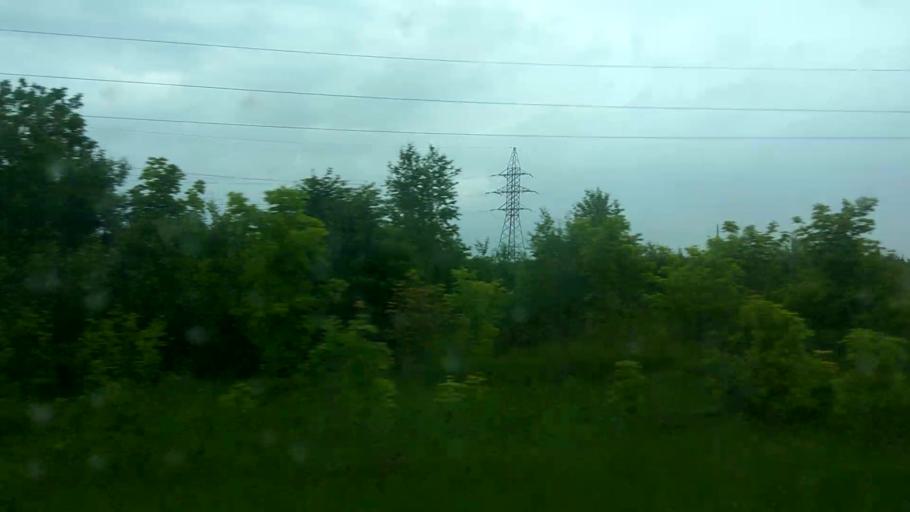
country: RU
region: Moskovskaya
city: Ozherel'ye
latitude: 54.8490
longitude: 38.2644
